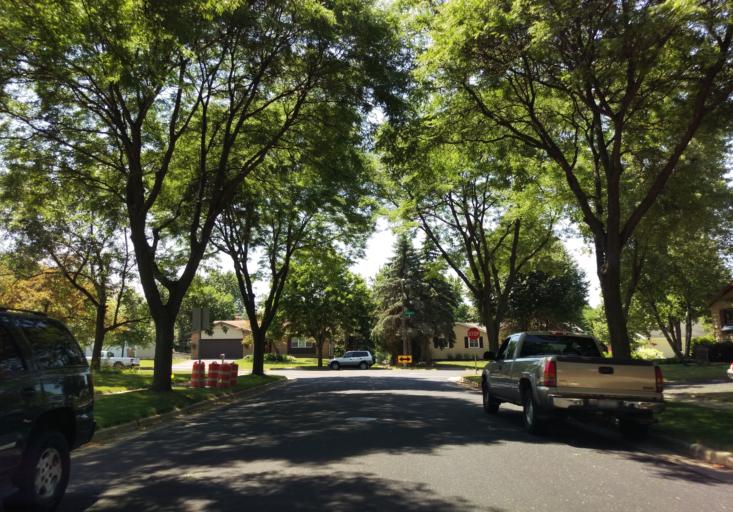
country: US
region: Wisconsin
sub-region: Dane County
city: Verona
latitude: 43.0202
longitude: -89.5031
